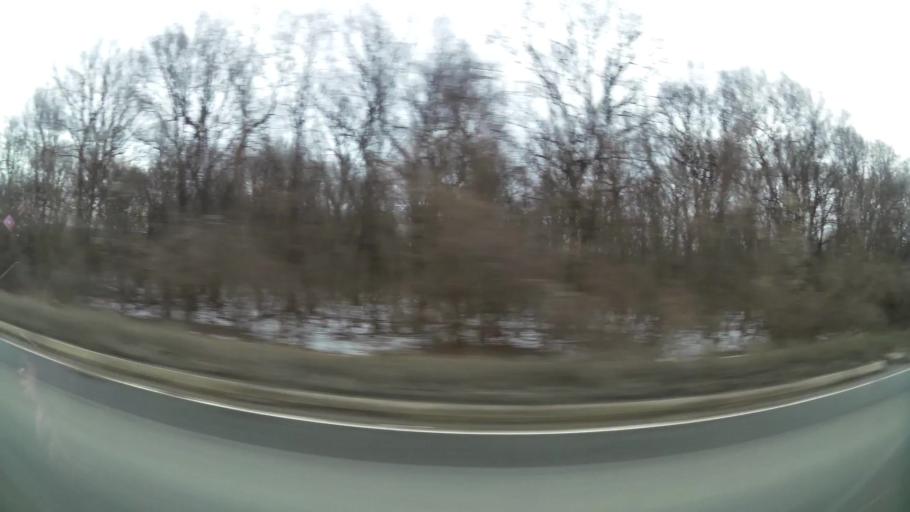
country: RS
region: Central Serbia
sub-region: Belgrade
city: Cukarica
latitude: 44.7669
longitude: 20.3923
